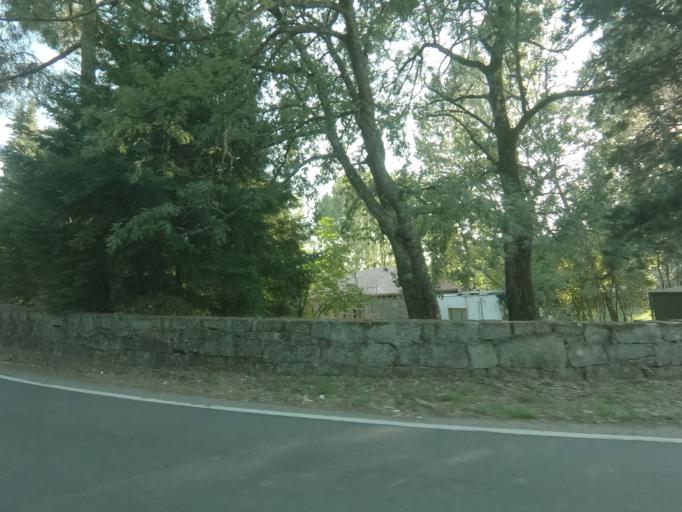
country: PT
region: Vila Real
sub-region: Vila Real
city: Vila Real
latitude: 41.2965
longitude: -7.7086
